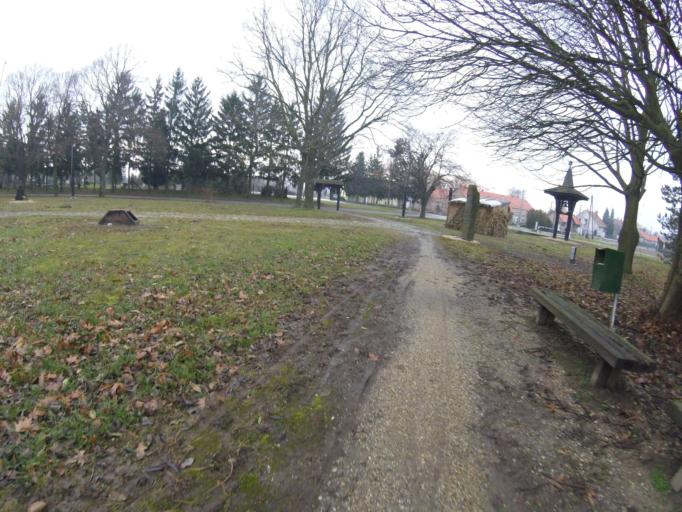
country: HU
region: Vas
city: Sarvar
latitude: 47.2435
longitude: 17.0239
